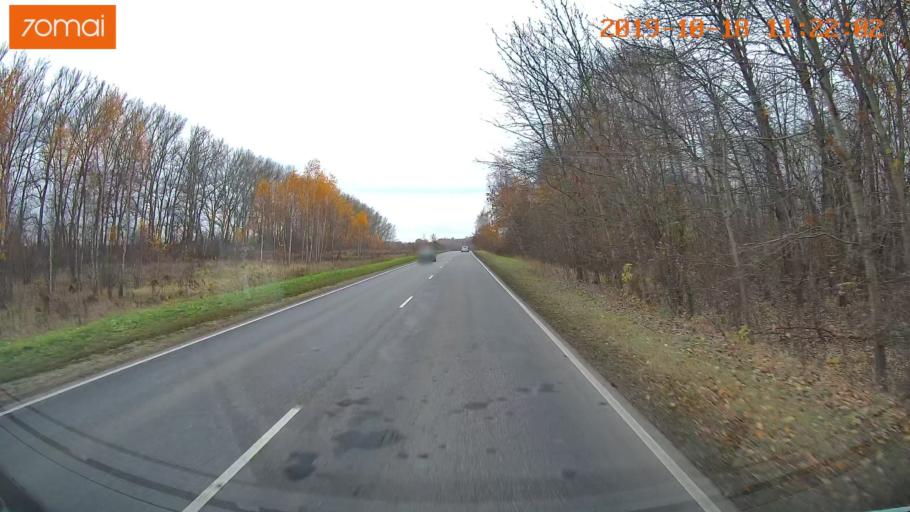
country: RU
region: Tula
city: Kimovsk
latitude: 54.0820
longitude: 38.5745
